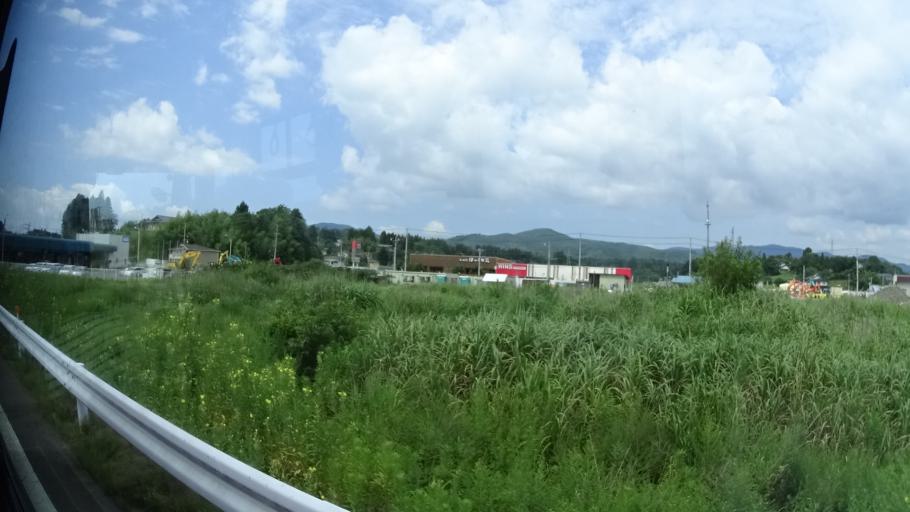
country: JP
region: Iwate
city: Ofunato
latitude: 38.8559
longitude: 141.5815
